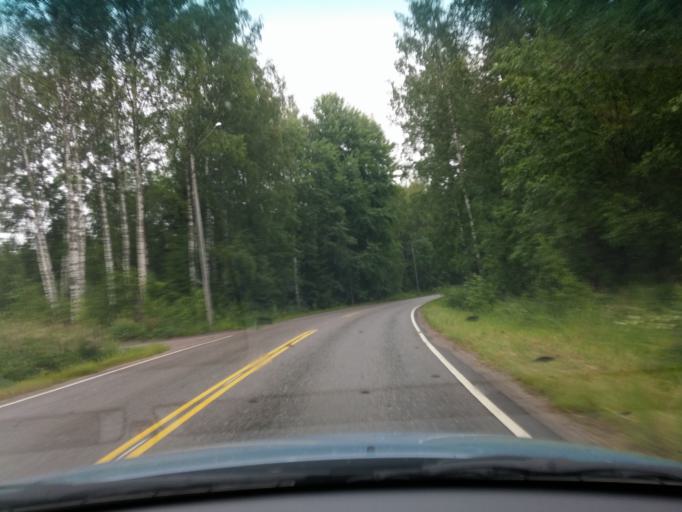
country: FI
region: Uusimaa
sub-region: Helsinki
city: Kauniainen
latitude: 60.3431
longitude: 24.7152
